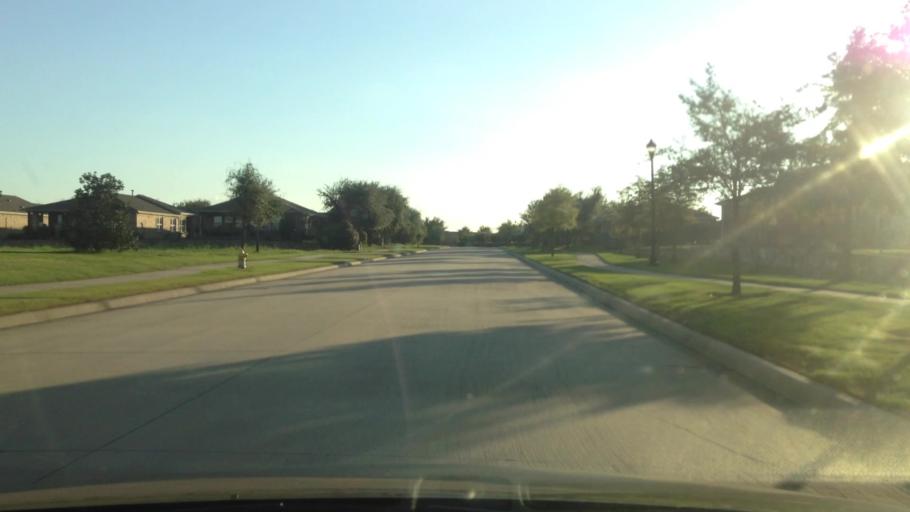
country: US
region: Texas
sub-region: Denton County
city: Little Elm
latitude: 33.1442
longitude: -96.9030
